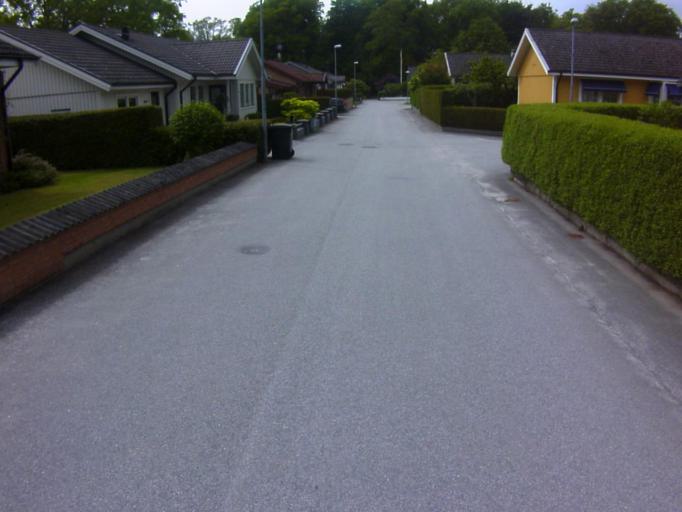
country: SE
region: Blekinge
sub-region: Solvesborgs Kommun
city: Soelvesborg
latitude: 56.0421
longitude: 14.5603
